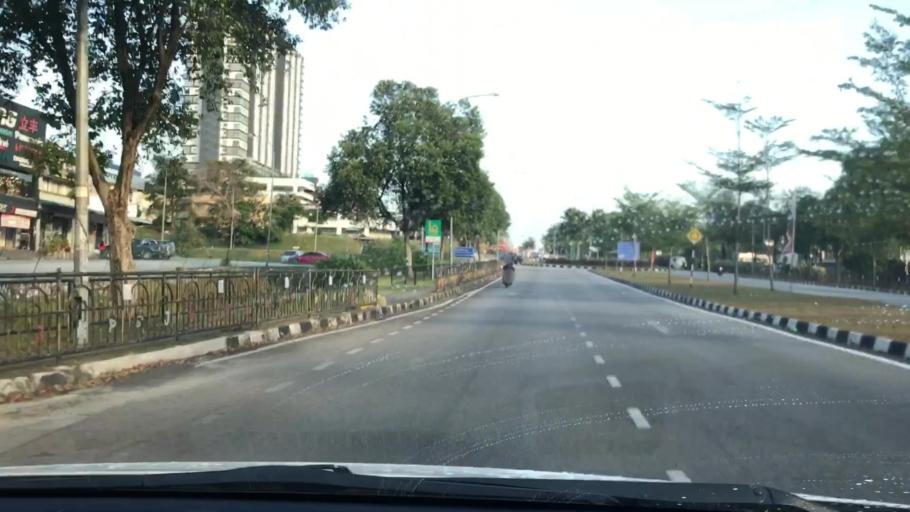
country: MY
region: Putrajaya
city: Putrajaya
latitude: 2.9934
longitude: 101.6740
